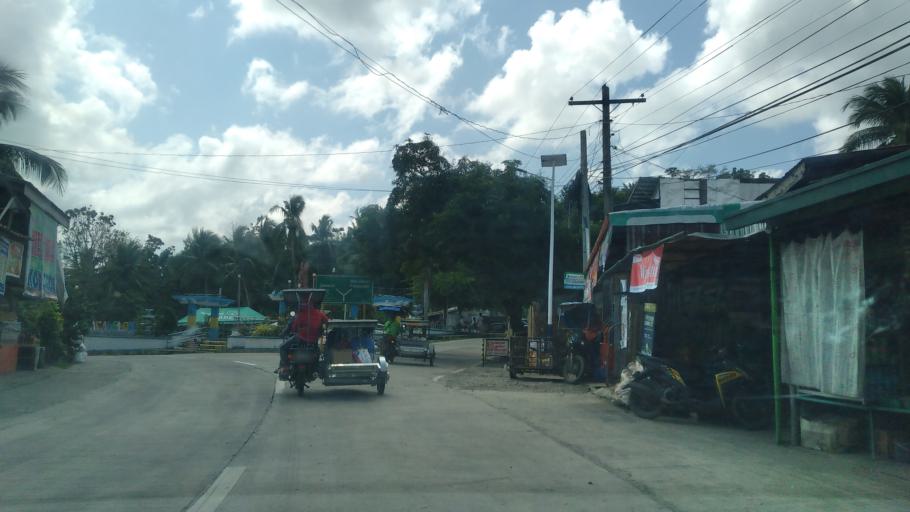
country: PH
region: Calabarzon
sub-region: Province of Quezon
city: Macalelon
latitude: 13.7558
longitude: 122.1439
